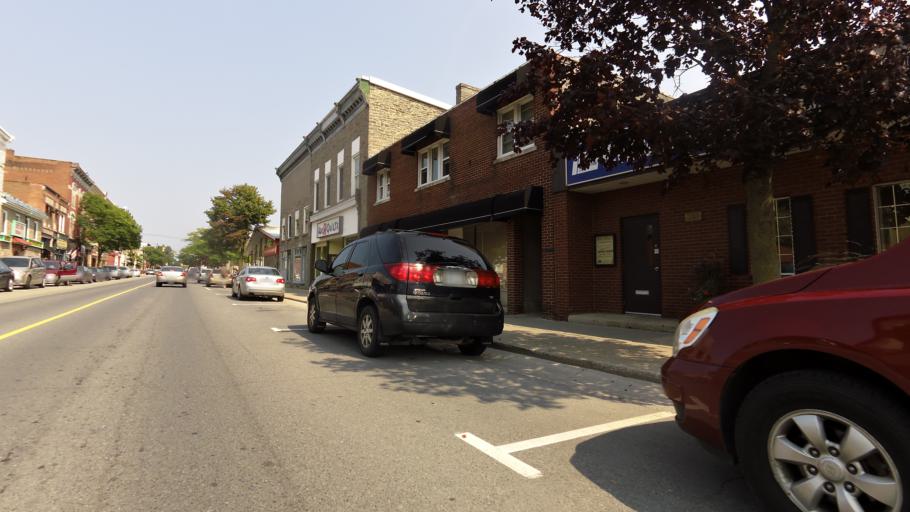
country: CA
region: Ontario
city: Prescott
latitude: 44.7086
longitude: -75.5157
